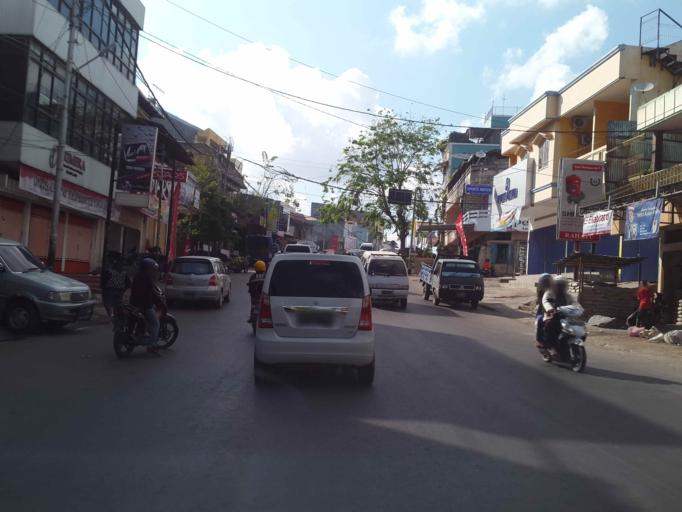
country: ID
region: East Nusa Tenggara
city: Kuanino
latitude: -10.1714
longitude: 123.5900
